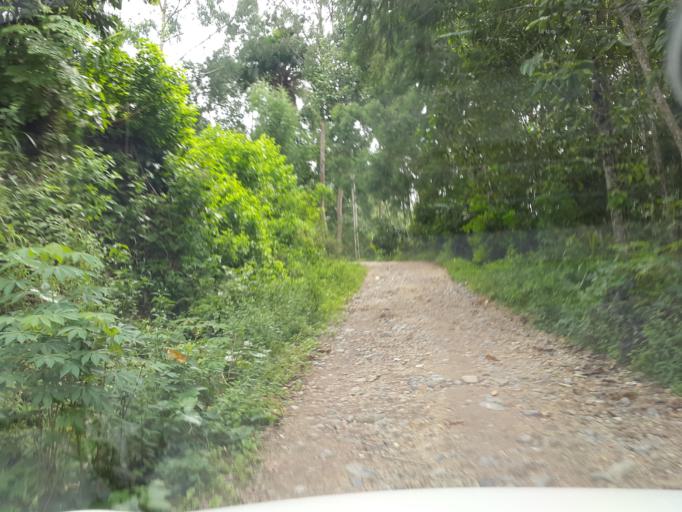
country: ID
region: South Sulawesi
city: Rantepang
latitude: -2.8699
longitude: 119.9477
